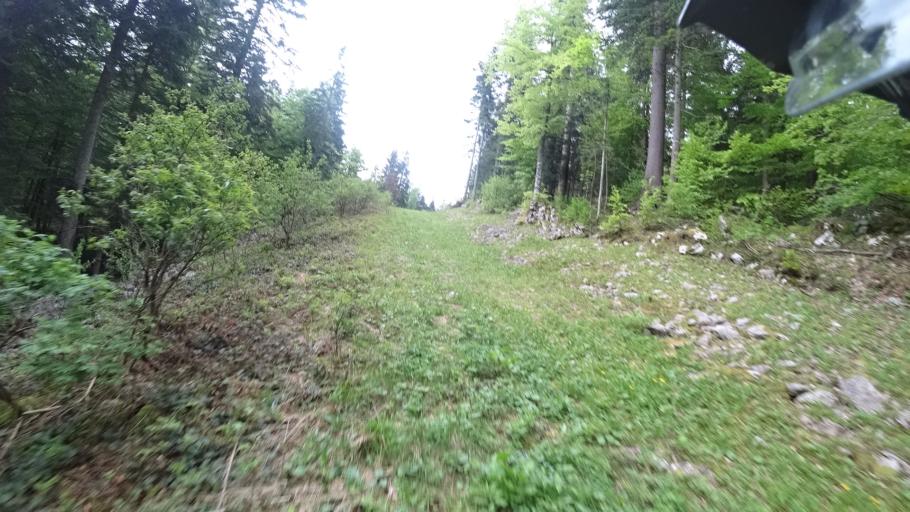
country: HR
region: Karlovacka
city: Plaski
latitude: 44.9577
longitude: 15.4135
